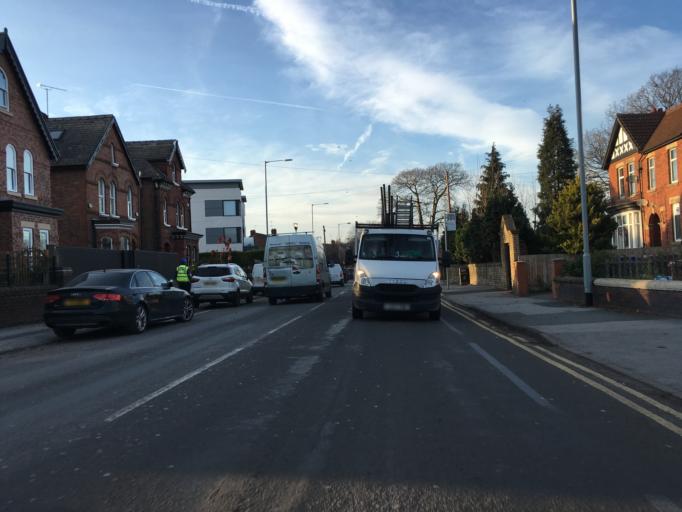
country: GB
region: England
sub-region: Borough of Stockport
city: Cheadle Heath
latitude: 53.4104
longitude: -2.1806
